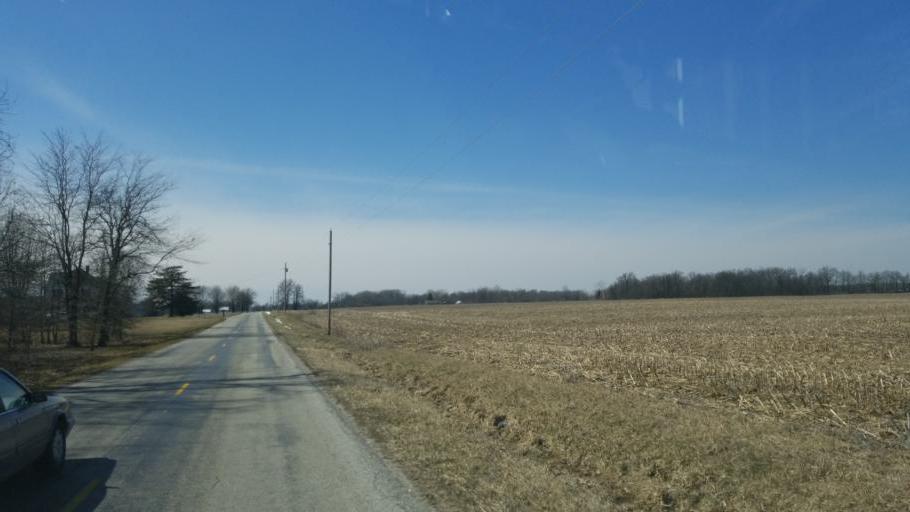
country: US
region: Ohio
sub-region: Crawford County
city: Bucyrus
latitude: 40.6750
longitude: -82.9274
